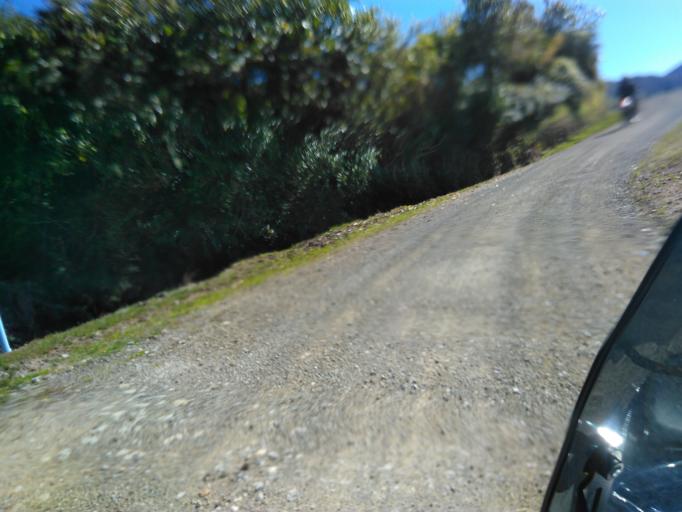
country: NZ
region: Bay of Plenty
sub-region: Opotiki District
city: Opotiki
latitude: -38.3579
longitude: 177.5898
